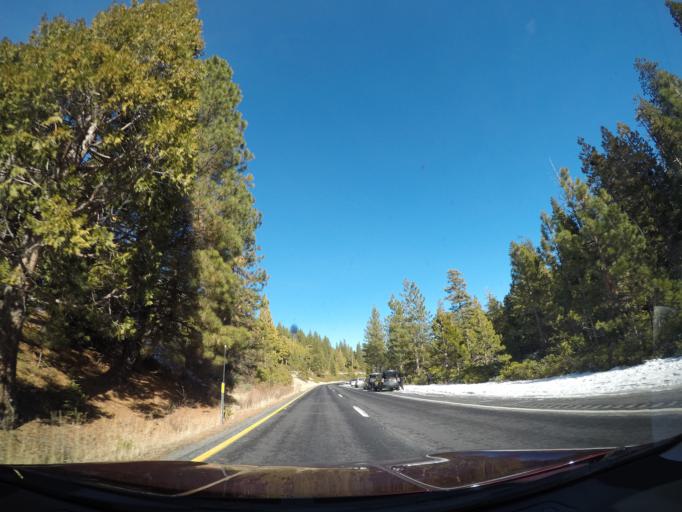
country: US
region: California
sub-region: Tuolumne County
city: Twain Harte
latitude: 38.1227
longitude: -120.1124
